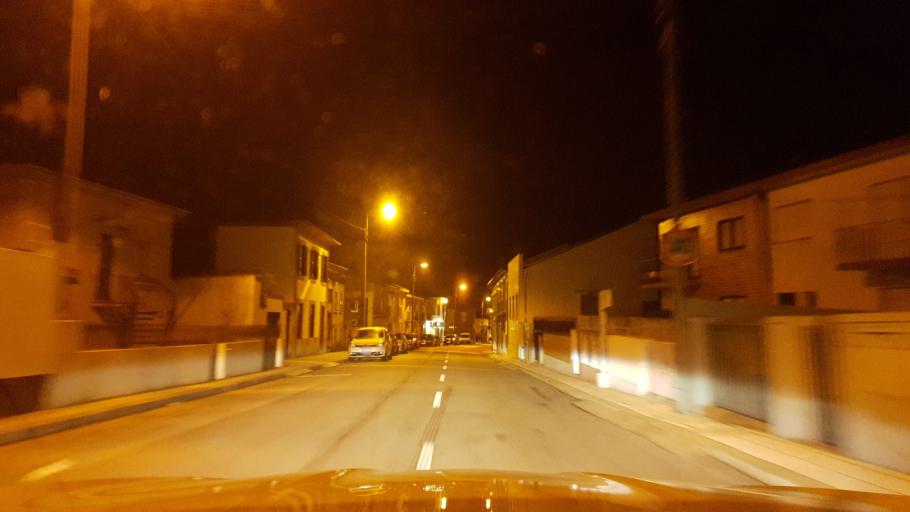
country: PT
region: Porto
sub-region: Maia
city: Leca do Bailio
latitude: 41.2150
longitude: -8.6353
